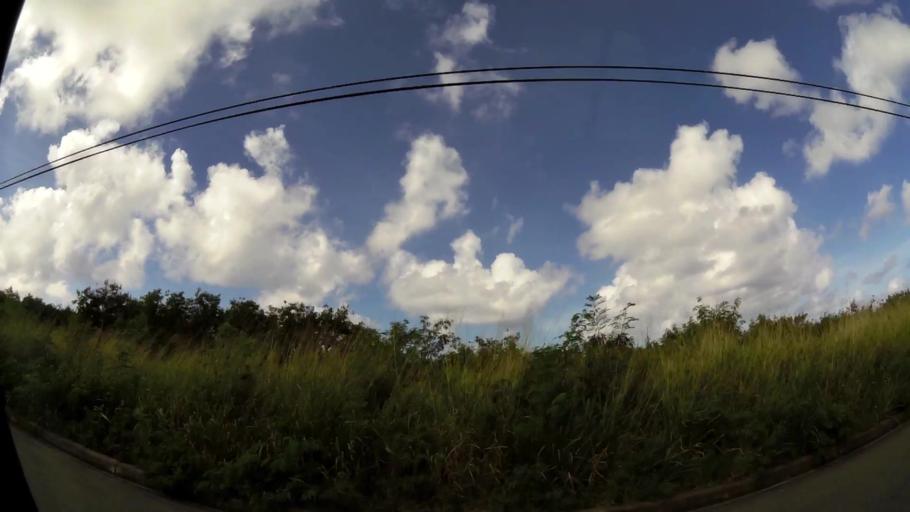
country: BB
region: Saint Lucy
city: Checker Hall
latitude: 13.2925
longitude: -59.6413
